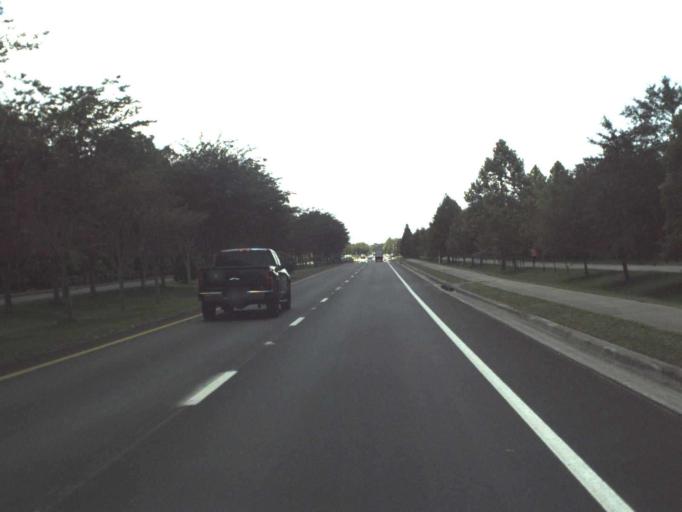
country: US
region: Florida
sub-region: Seminole County
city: Winter Springs
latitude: 28.7055
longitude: -81.2768
